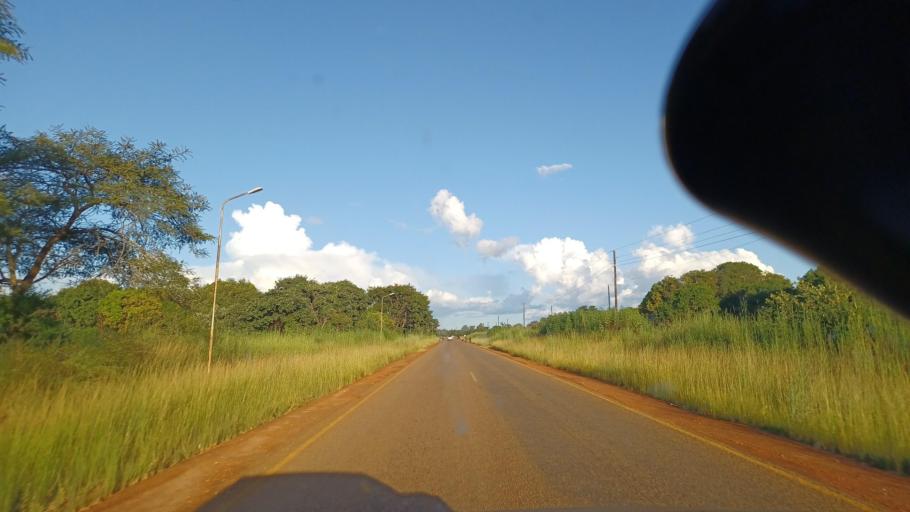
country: ZM
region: North-Western
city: Kalengwa
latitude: -13.1396
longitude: 25.0174
